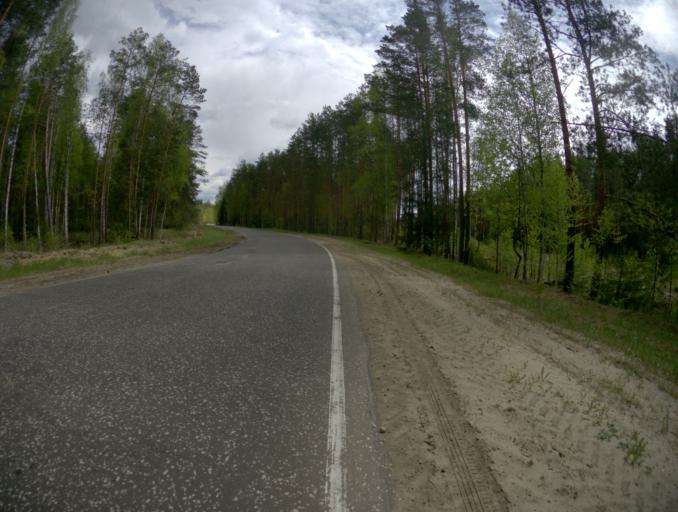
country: RU
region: Vladimir
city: Velikodvorskiy
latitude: 55.3959
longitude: 40.6975
